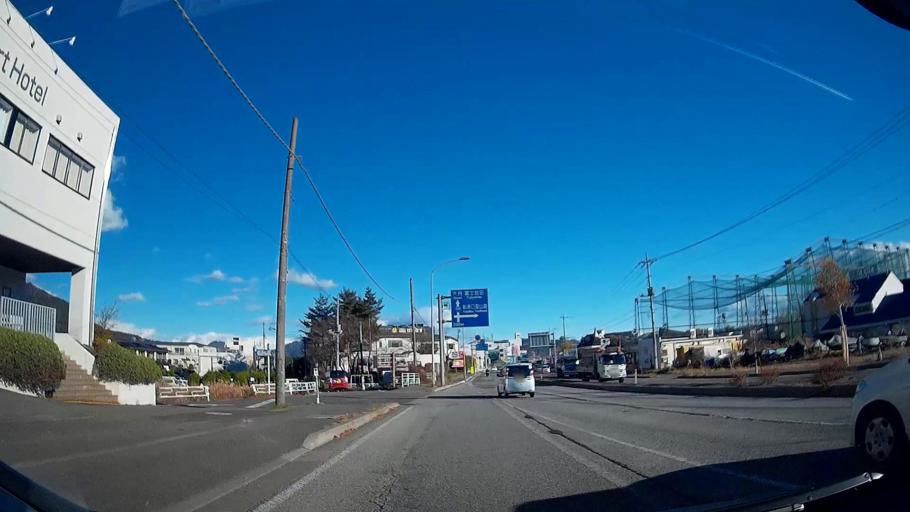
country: JP
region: Yamanashi
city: Fujikawaguchiko
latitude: 35.4914
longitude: 138.7590
